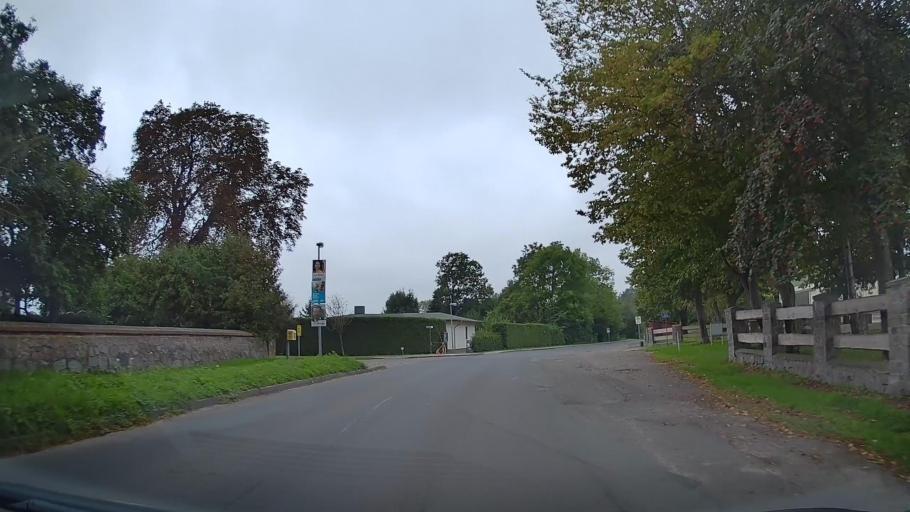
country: DE
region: Mecklenburg-Vorpommern
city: Tarnow
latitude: 53.7855
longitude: 12.0861
